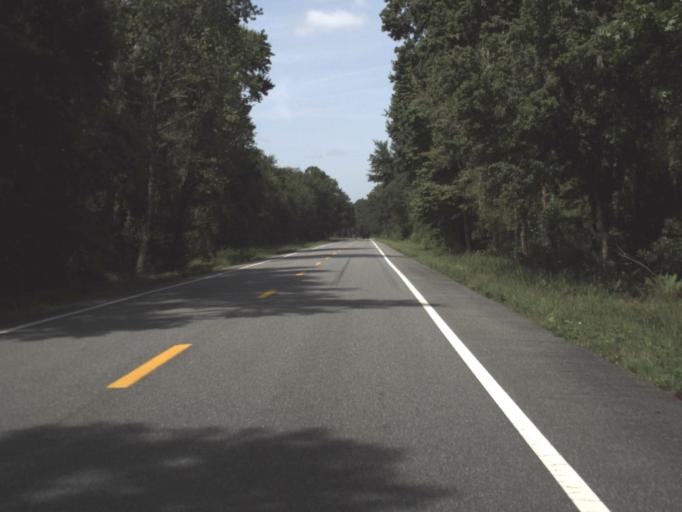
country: US
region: Florida
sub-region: Lafayette County
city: Mayo
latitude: 29.9208
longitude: -83.2845
